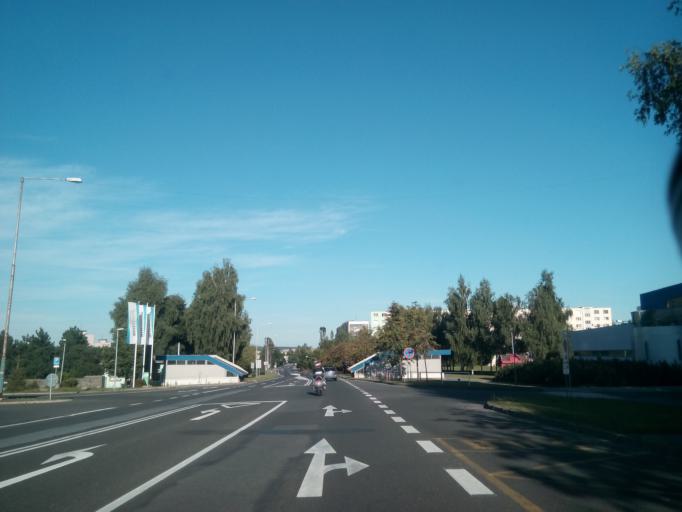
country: SK
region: Presovsky
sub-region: Okres Poprad
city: Poprad
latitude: 49.0504
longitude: 20.2991
